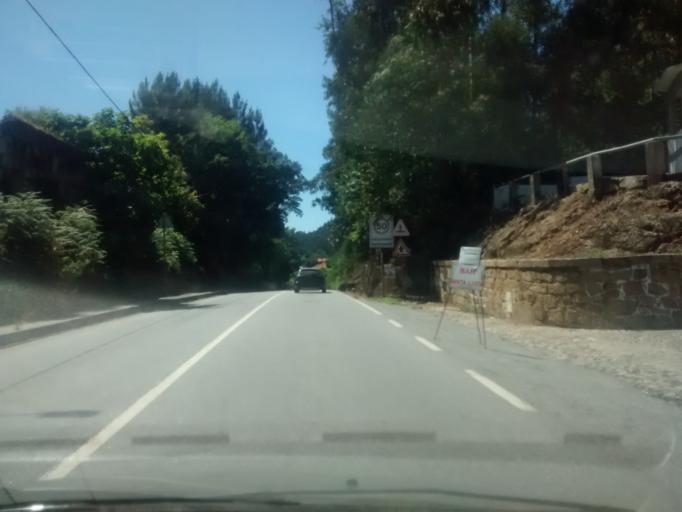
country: PT
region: Braga
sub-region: Barcelos
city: Galegos
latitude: 41.5306
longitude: -8.5408
